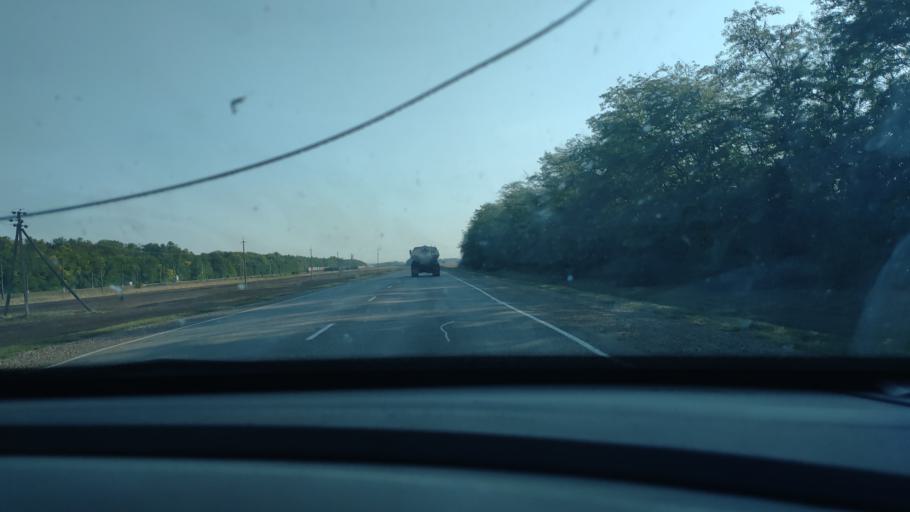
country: RU
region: Krasnodarskiy
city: Starominskaya
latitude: 46.4810
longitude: 39.0516
